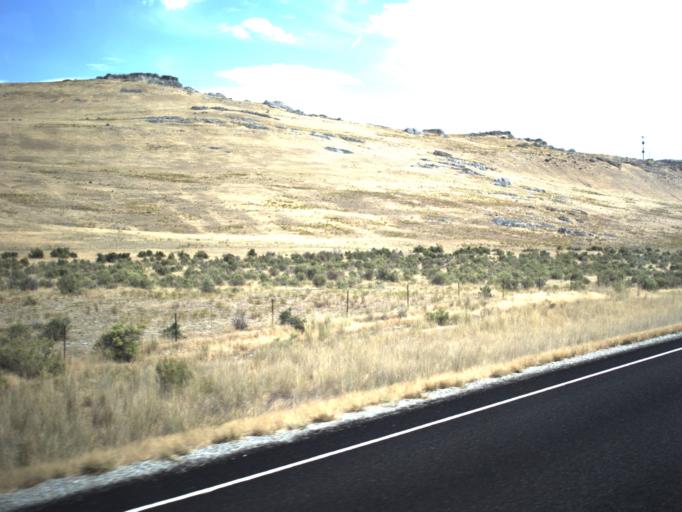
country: US
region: Utah
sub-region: Box Elder County
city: Tremonton
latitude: 41.6194
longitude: -112.3848
